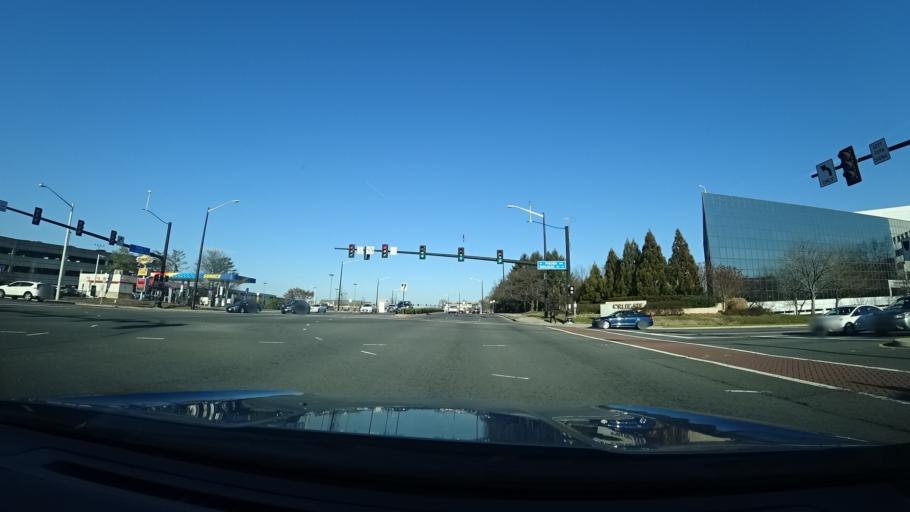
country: US
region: Virginia
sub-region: Fairfax County
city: Herndon
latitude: 38.9591
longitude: -77.4020
